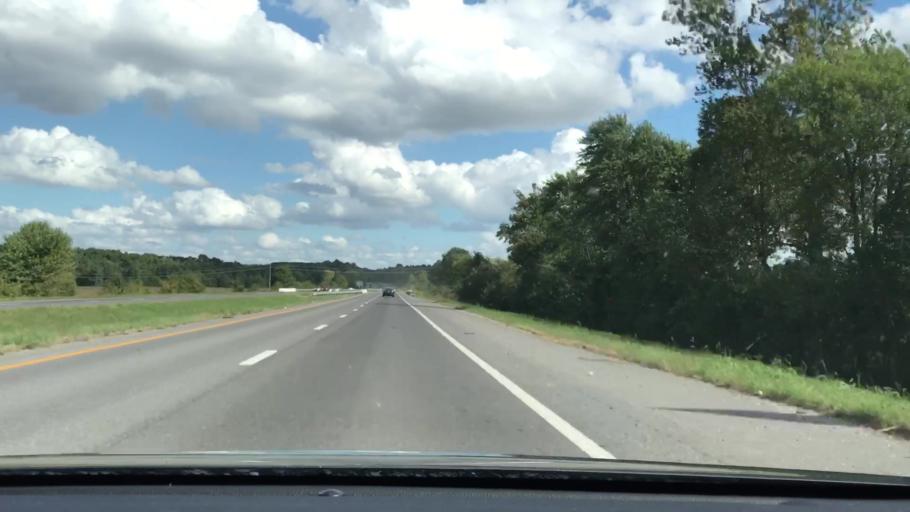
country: US
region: Kentucky
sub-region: Graves County
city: Mayfield
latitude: 36.7692
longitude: -88.6300
